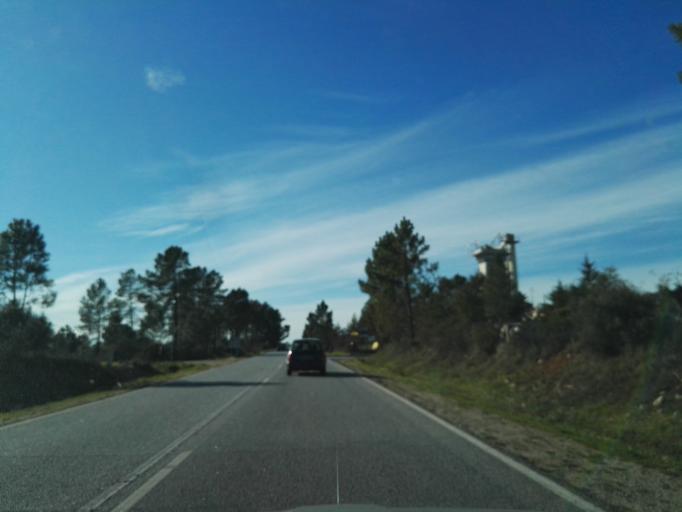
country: PT
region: Santarem
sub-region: Abrantes
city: Alferrarede
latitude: 39.4753
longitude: -8.0747
